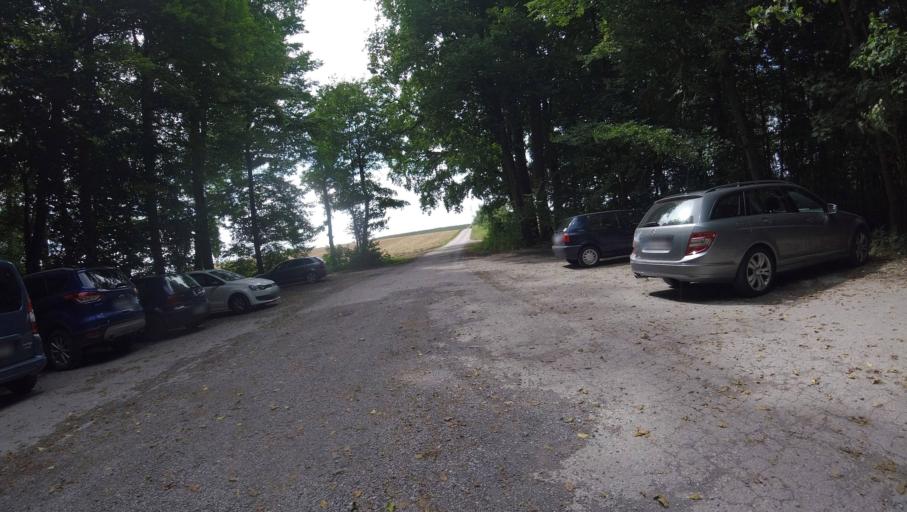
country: DE
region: Baden-Wuerttemberg
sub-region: Regierungsbezirk Stuttgart
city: Kirchberg an der Murr
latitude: 48.9668
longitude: 9.3574
